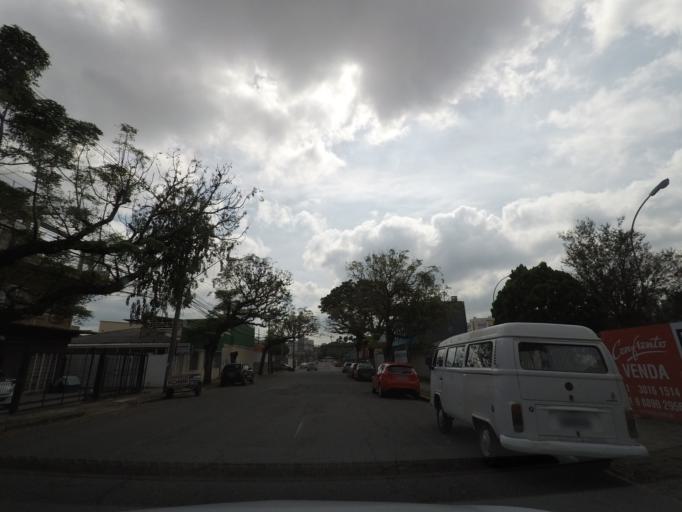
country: BR
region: Parana
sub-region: Curitiba
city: Curitiba
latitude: -25.4530
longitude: -49.2551
